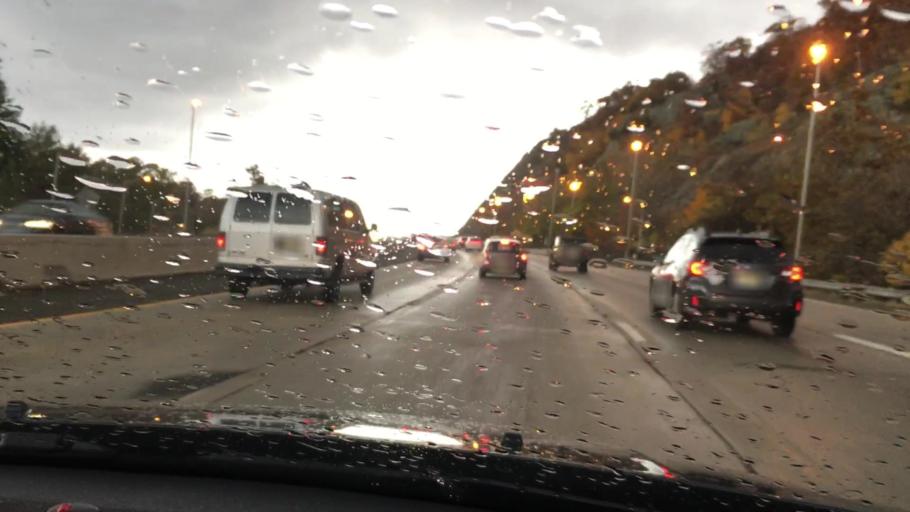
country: US
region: New Jersey
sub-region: Bergen County
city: Oakland
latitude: 41.0284
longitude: -74.2526
